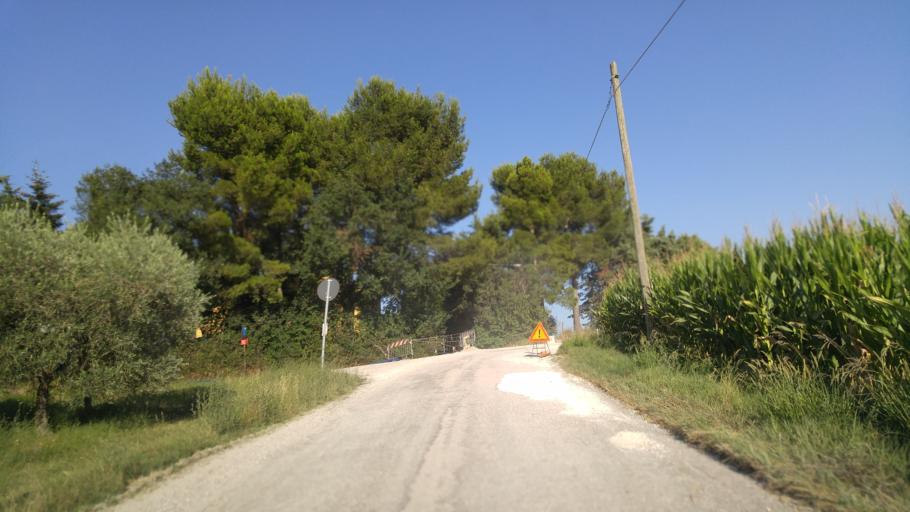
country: IT
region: The Marches
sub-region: Provincia di Pesaro e Urbino
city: Mombaroccio
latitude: 43.8111
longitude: 12.8876
